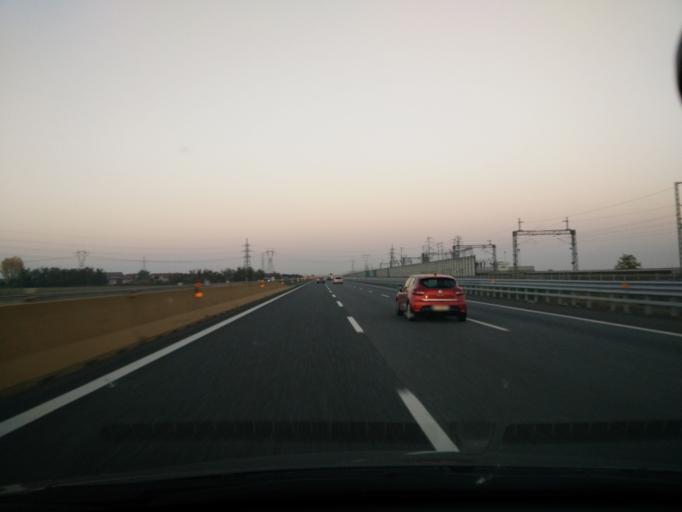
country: IT
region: Piedmont
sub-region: Provincia di Vercelli
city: Cigliano
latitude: 45.2781
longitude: 8.0260
